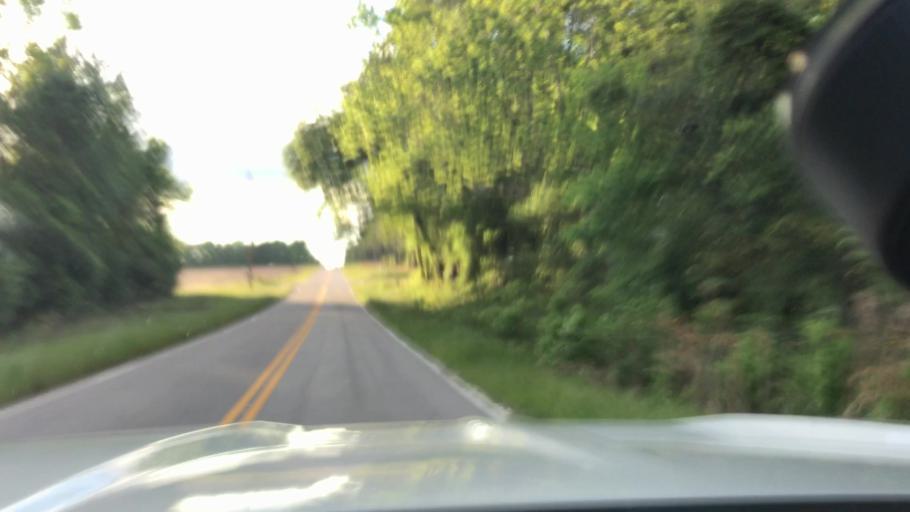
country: US
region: South Carolina
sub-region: Bamberg County
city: Denmark
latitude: 33.4645
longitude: -81.1576
